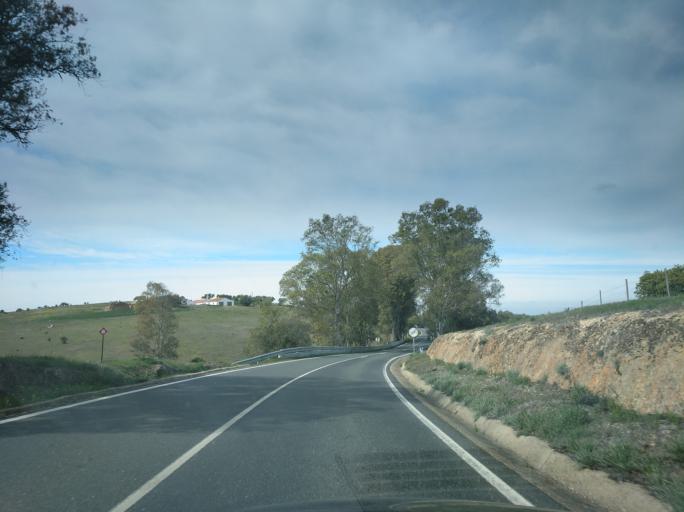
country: PT
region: Beja
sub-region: Mertola
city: Mertola
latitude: 37.7191
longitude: -7.7592
